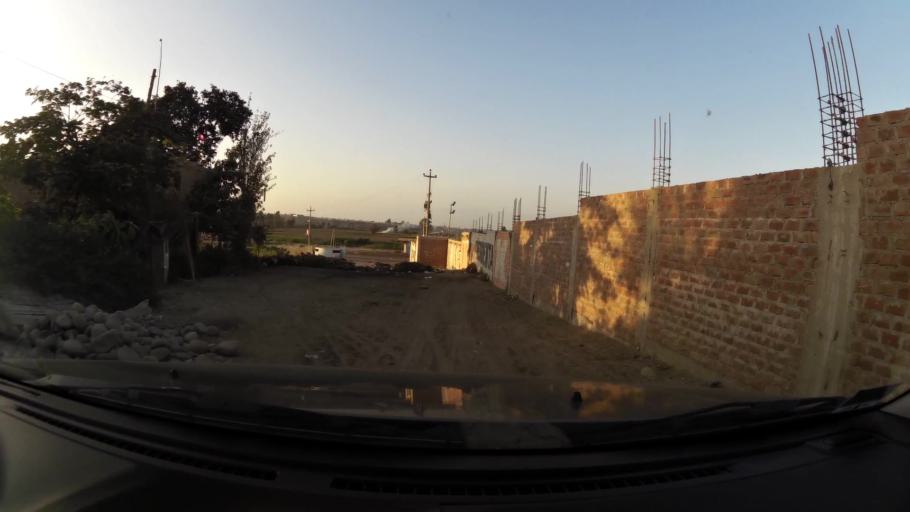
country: PE
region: Ica
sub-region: Provincia de Pisco
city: Villa Tupac Amaru
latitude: -13.6987
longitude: -76.1529
